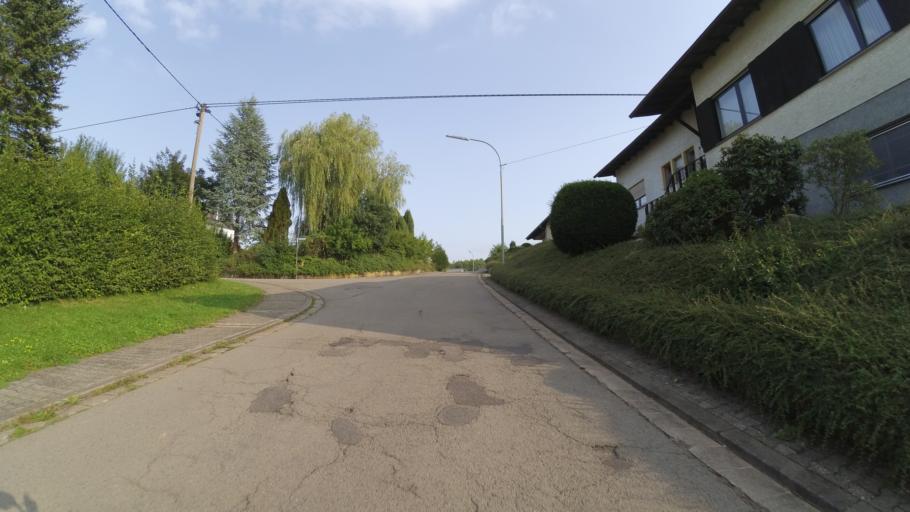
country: DE
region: Saarland
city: Wadern
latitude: 49.5347
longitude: 6.8893
